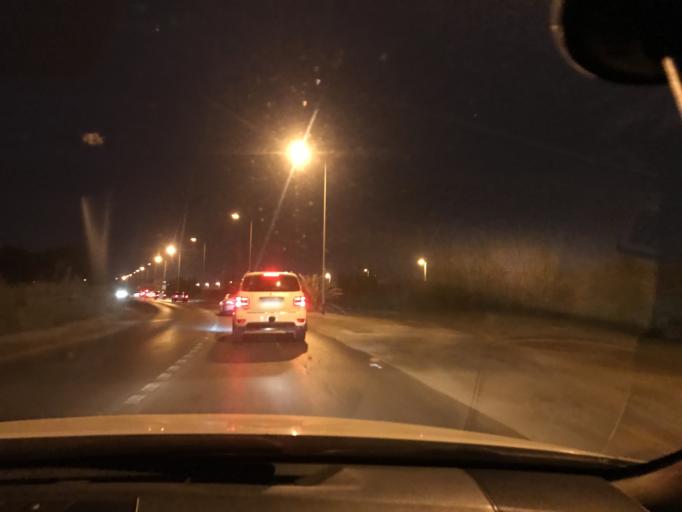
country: BH
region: Muharraq
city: Al Muharraq
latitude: 26.2814
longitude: 50.6190
